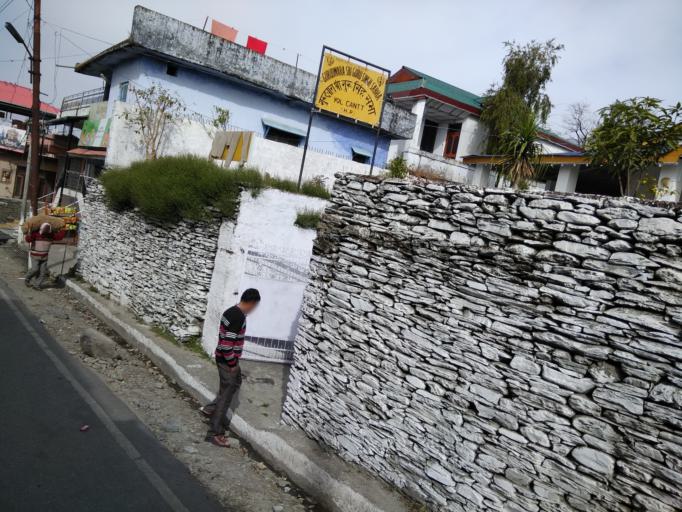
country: IN
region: Himachal Pradesh
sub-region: Kangra
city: Dharmsala
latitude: 32.1837
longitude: 76.3733
